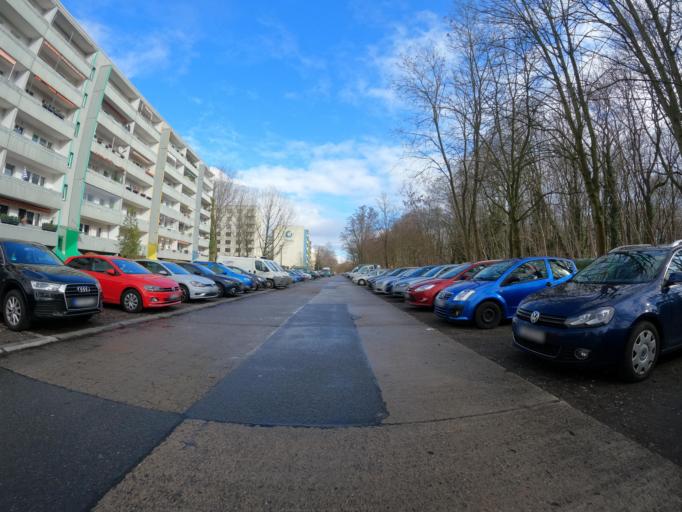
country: DE
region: Berlin
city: Marzahn
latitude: 52.5249
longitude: 13.5673
